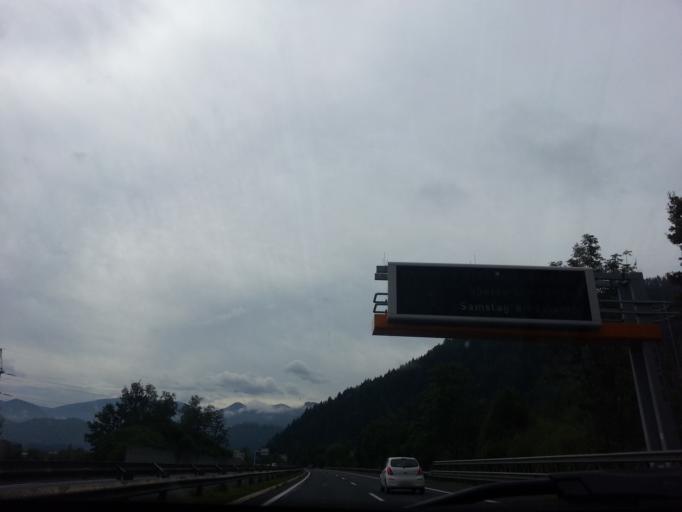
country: AT
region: Styria
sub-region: Politischer Bezirk Leoben
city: Traboch
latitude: 47.3572
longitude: 15.0009
